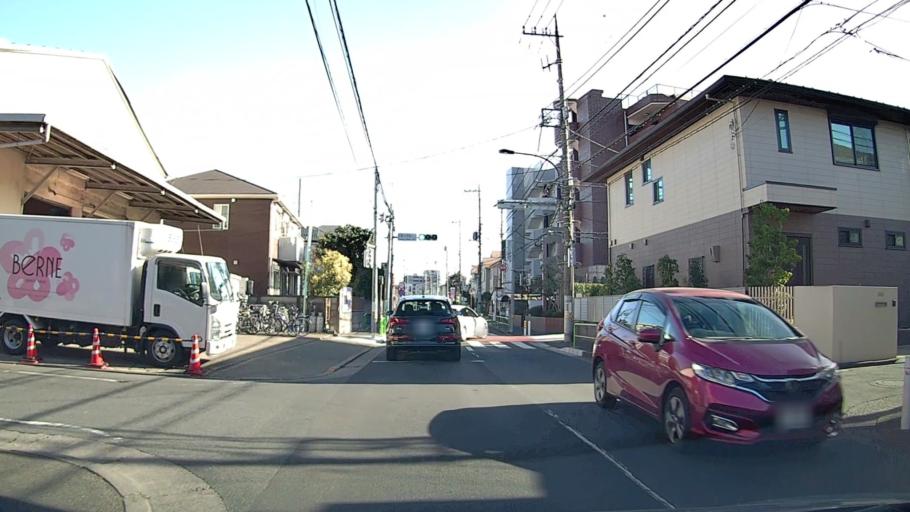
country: JP
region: Saitama
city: Wako
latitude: 35.7525
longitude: 139.6147
